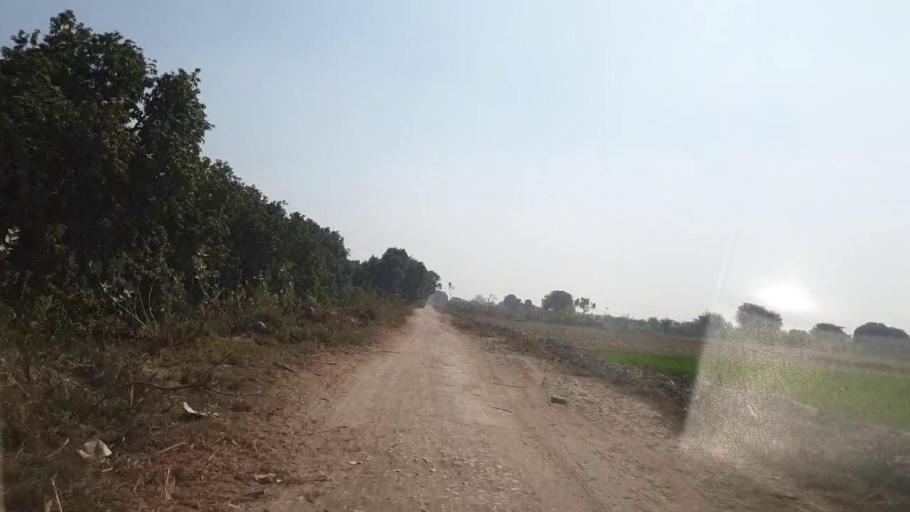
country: PK
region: Sindh
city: Matiari
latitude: 25.5106
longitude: 68.4622
